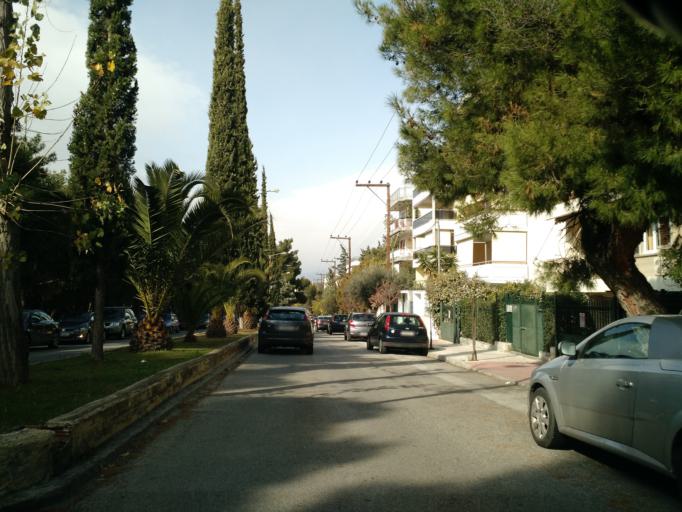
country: GR
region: Attica
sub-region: Nomarchia Athinas
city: Papagou
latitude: 37.9935
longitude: 23.7905
